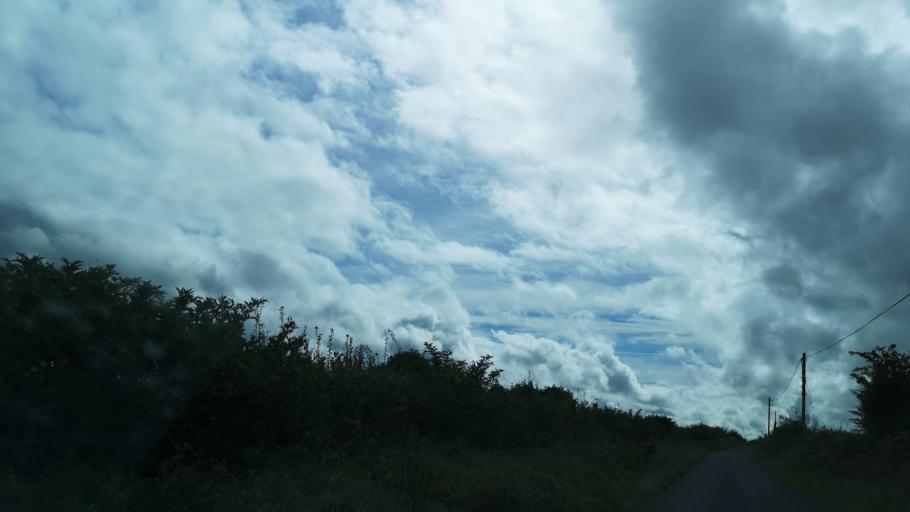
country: IE
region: Connaught
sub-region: County Galway
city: Athenry
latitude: 53.2818
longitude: -8.6685
